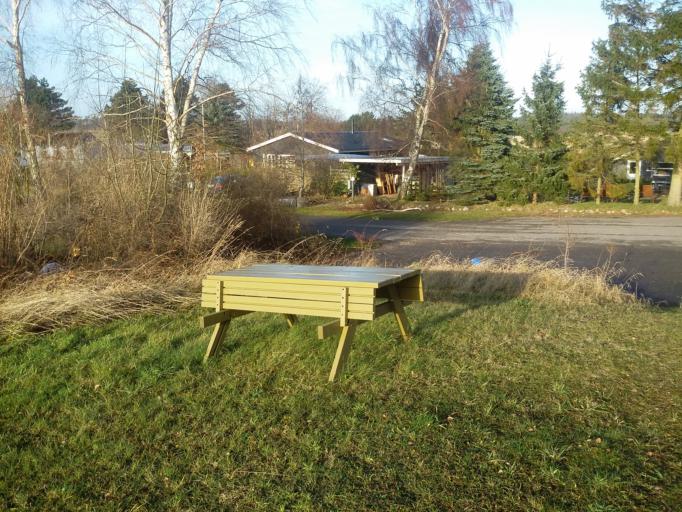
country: DK
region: Zealand
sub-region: Roskilde Kommune
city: Jyllinge
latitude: 55.7776
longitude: 12.0539
